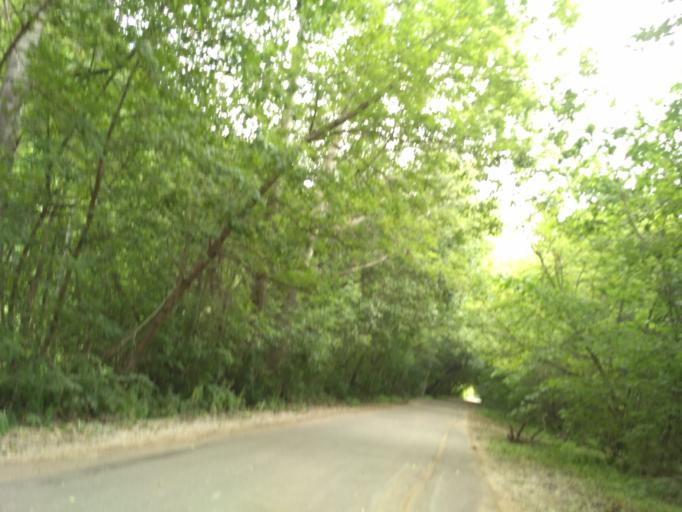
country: RU
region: Nizjnij Novgorod
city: Nizhniy Novgorod
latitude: 56.2948
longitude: 43.9678
